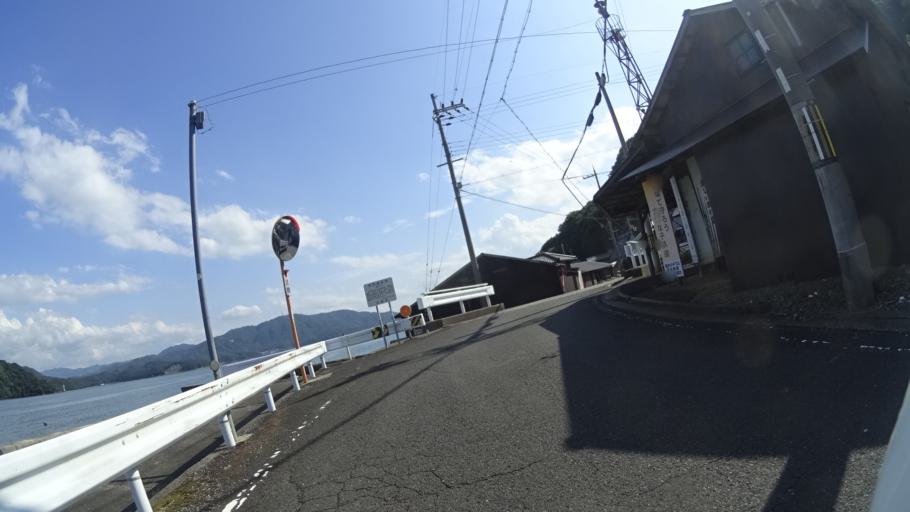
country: JP
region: Kyoto
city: Maizuru
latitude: 35.4980
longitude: 135.3326
